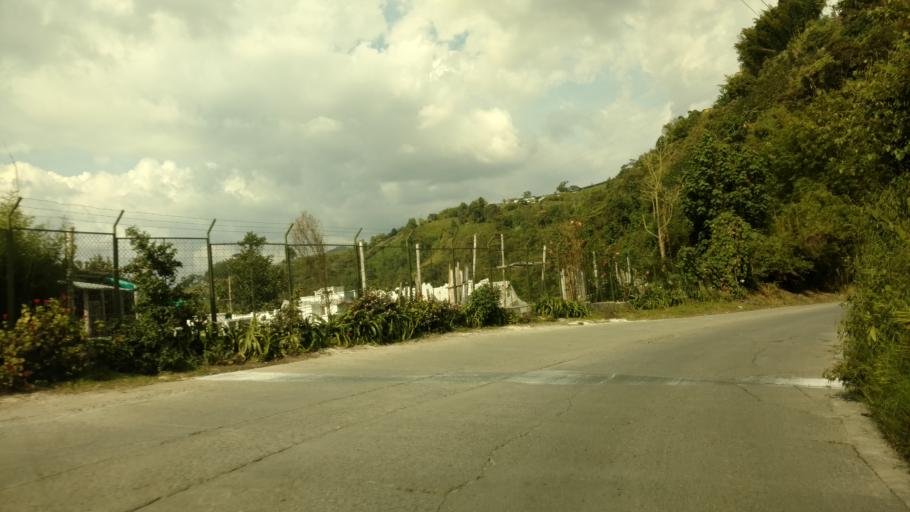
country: CO
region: Caldas
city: Manizales
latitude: 5.0882
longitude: -75.5182
